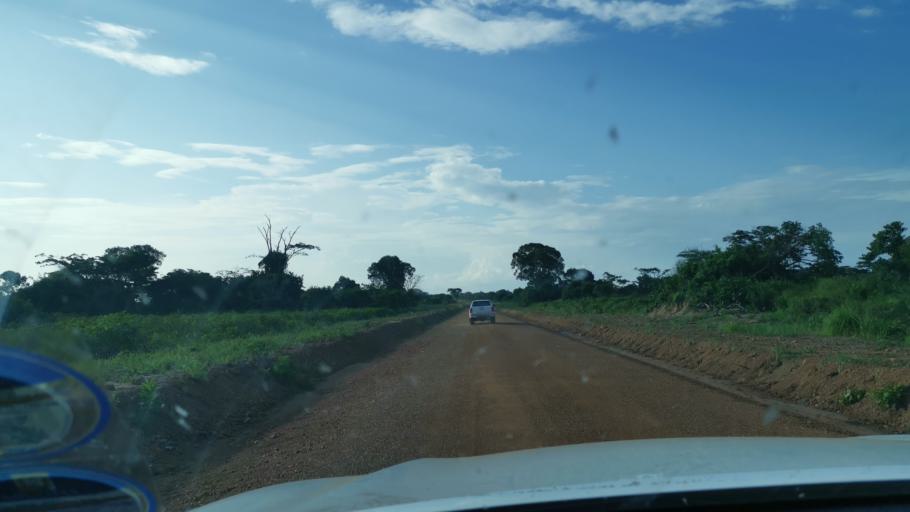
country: ZM
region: Luapula
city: Samfya
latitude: -11.1114
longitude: 29.5764
